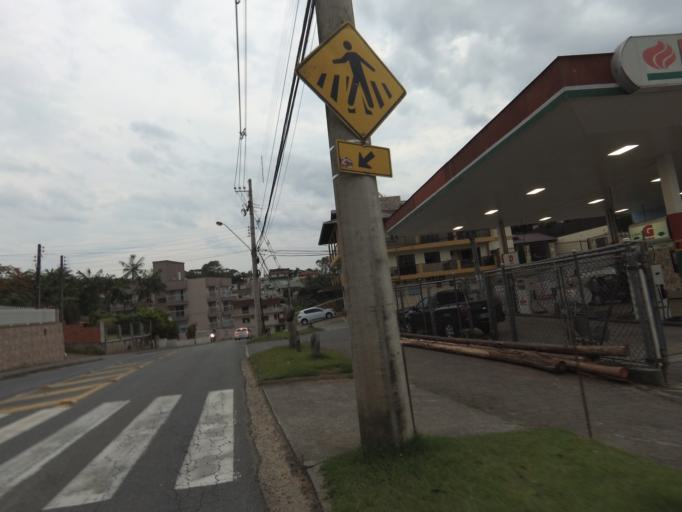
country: BR
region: Santa Catarina
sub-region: Blumenau
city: Blumenau
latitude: -26.8767
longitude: -49.0587
